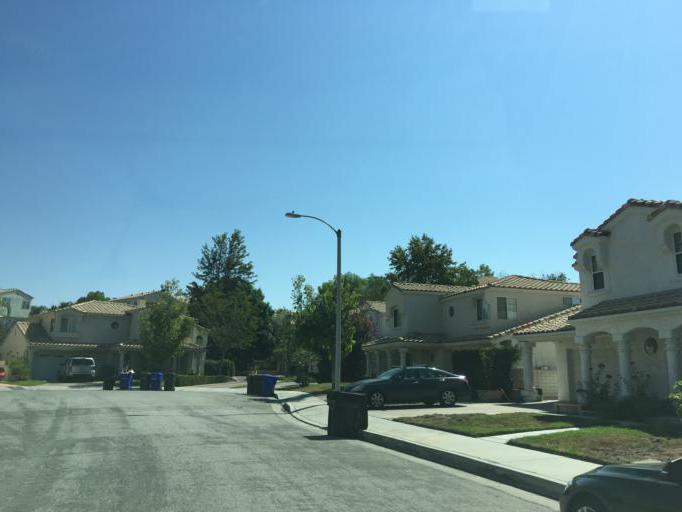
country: US
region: California
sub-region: Los Angeles County
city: Santa Clarita
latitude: 34.3864
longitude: -118.5786
